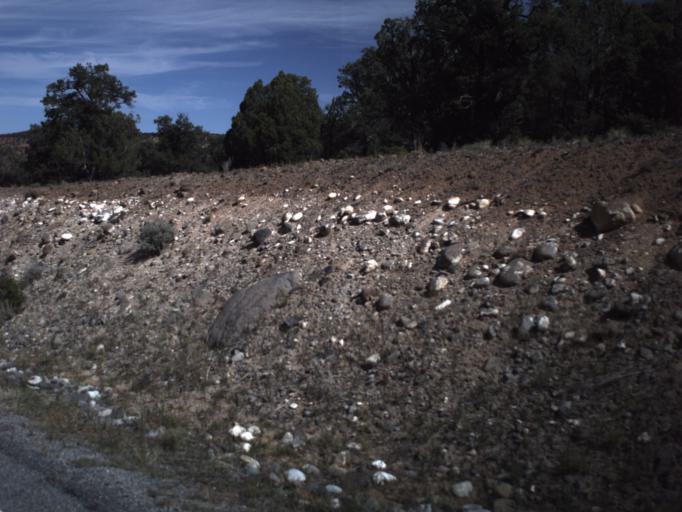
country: US
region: Utah
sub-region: Wayne County
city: Loa
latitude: 38.2039
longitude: -111.3489
